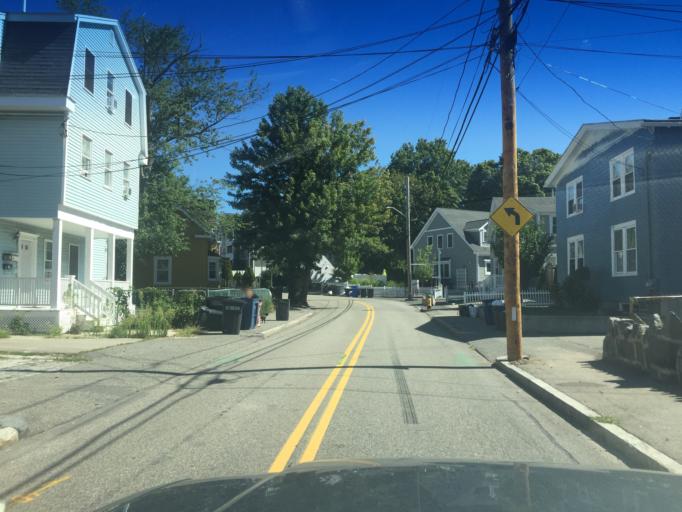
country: US
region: Massachusetts
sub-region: Norfolk County
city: Quincy
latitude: 42.2470
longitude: -70.9876
